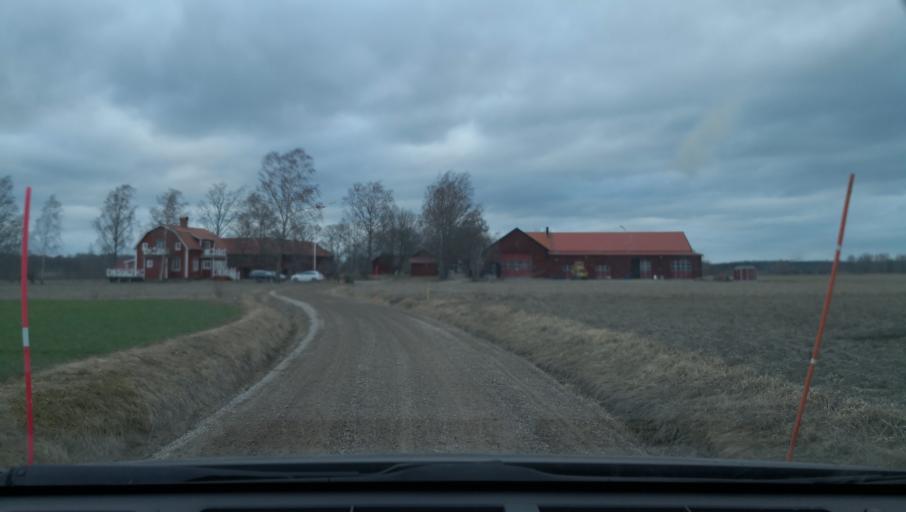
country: SE
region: Vaestmanland
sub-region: Kopings Kommun
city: Kolsva
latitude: 59.5339
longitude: 15.8929
